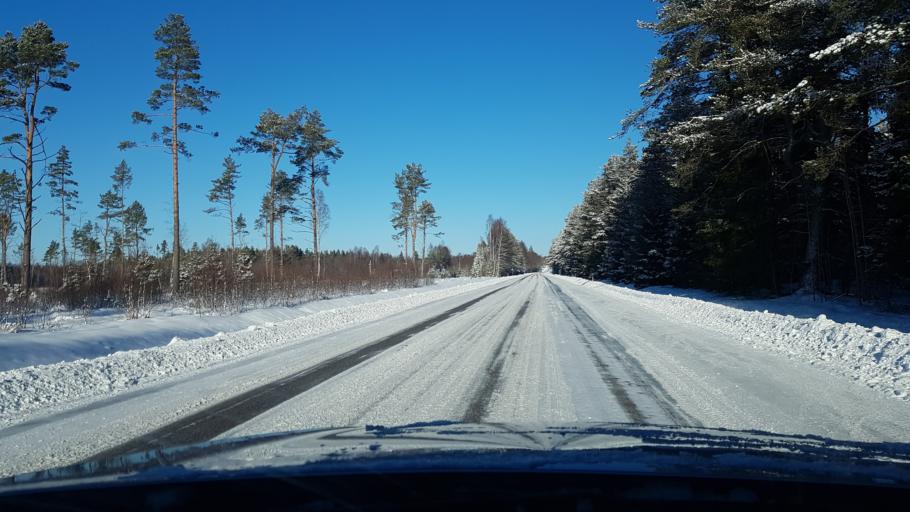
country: EE
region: Hiiumaa
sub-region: Kaerdla linn
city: Kardla
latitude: 58.9083
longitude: 22.7916
